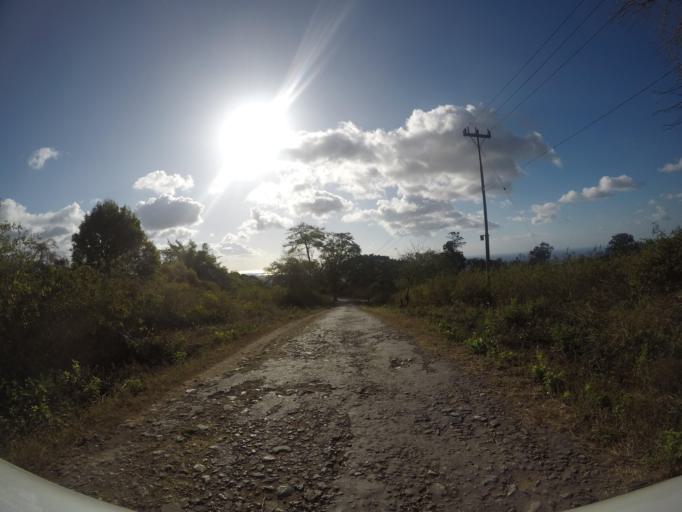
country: TL
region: Lautem
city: Lospalos
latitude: -8.4392
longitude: 126.8597
